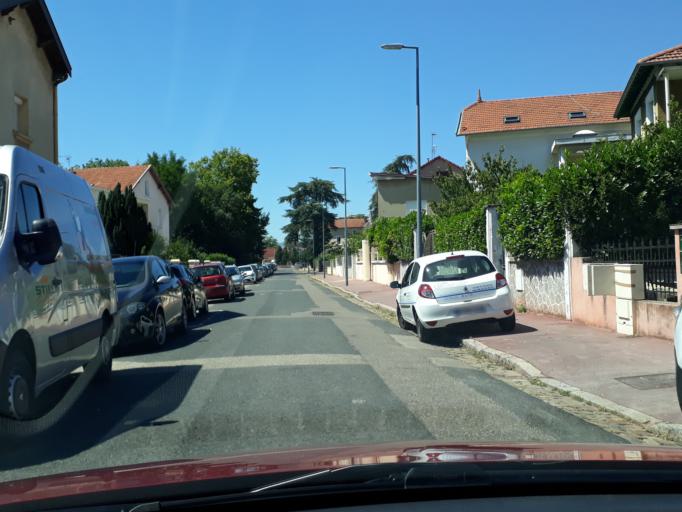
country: FR
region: Rhone-Alpes
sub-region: Departement du Rhone
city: Bron
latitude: 45.7201
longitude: 4.8927
